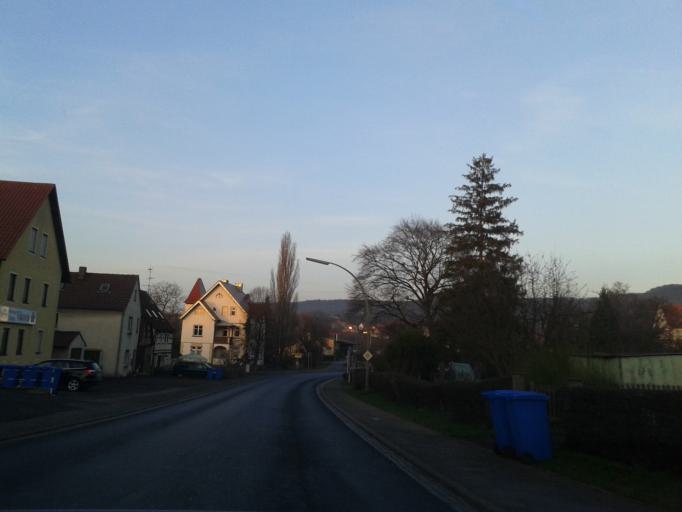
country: DE
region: Bavaria
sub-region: Regierungsbezirk Unterfranken
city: Hassfurt
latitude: 50.0820
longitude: 10.5663
